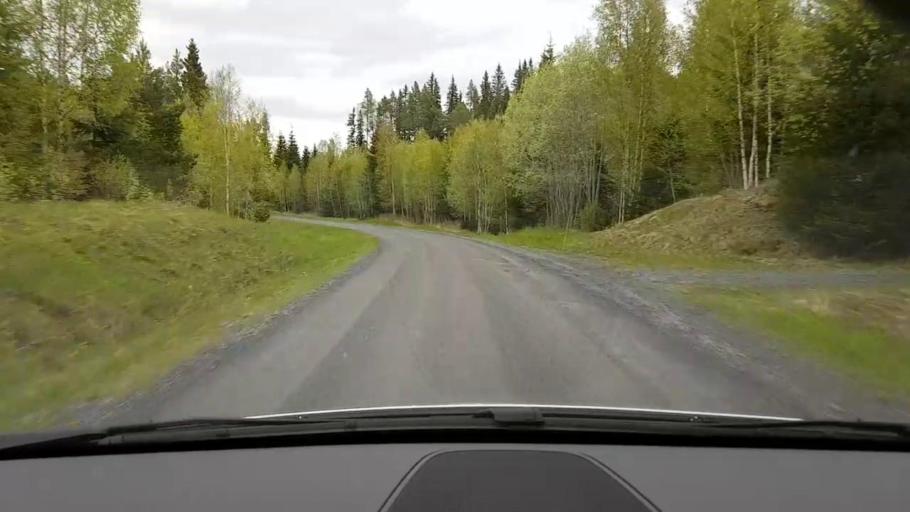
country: SE
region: Jaemtland
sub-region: Krokoms Kommun
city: Krokom
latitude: 63.2982
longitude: 14.3957
